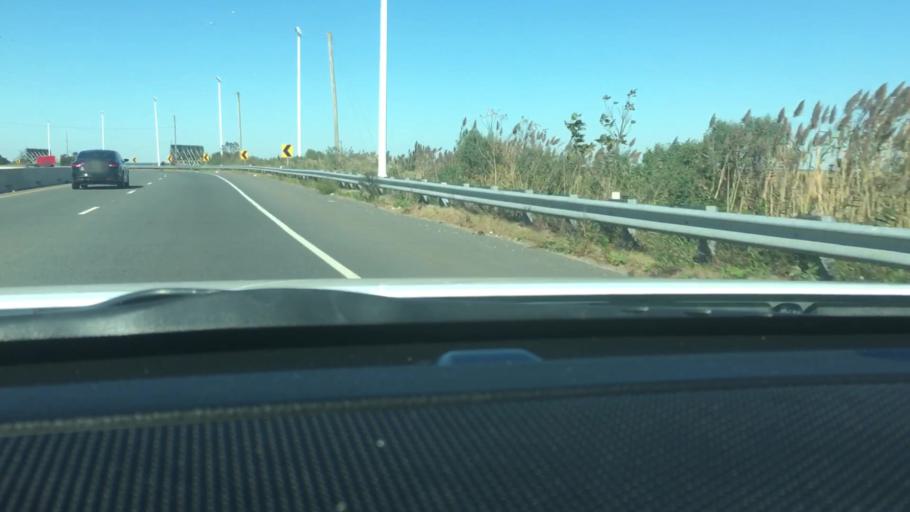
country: US
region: New Jersey
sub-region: Atlantic County
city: Atlantic City
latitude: 39.3832
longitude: -74.4596
